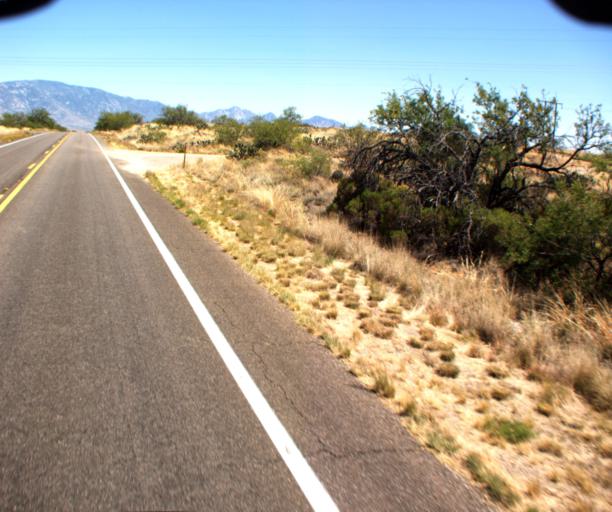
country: US
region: Arizona
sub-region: Pima County
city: Catalina
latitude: 32.6022
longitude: -110.9815
